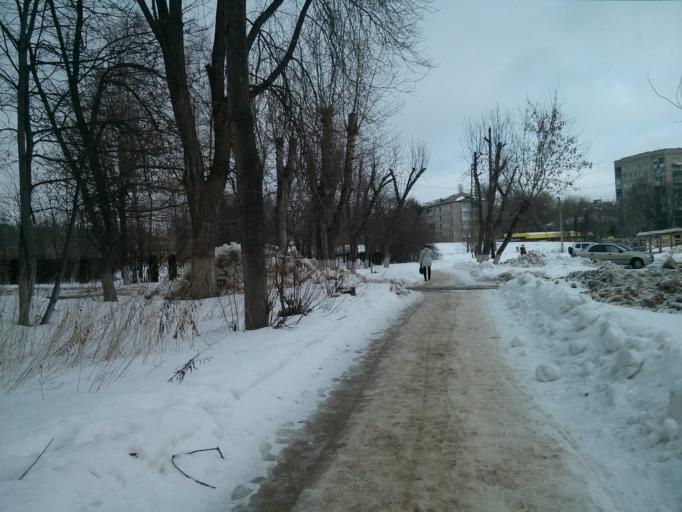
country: RU
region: Vladimir
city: Murom
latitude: 55.5629
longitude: 42.0573
